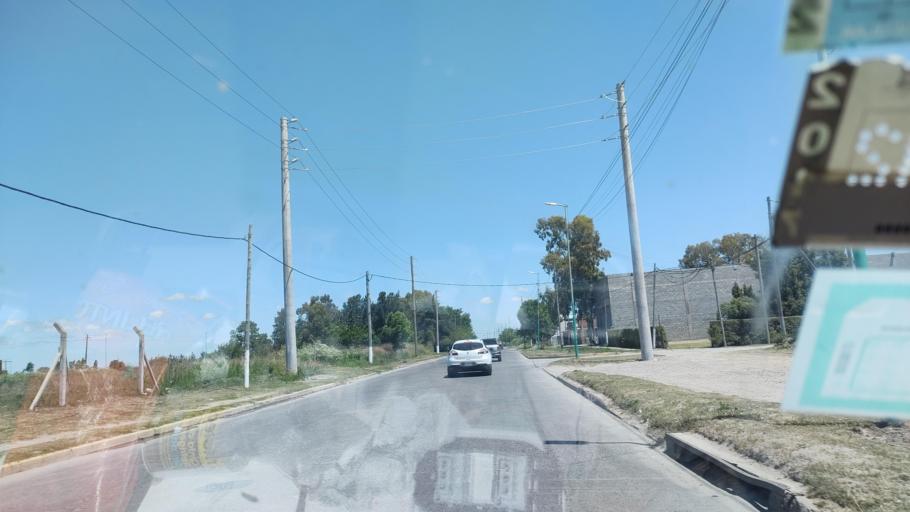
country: AR
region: Buenos Aires
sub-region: Partido de Berisso
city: Berisso
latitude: -34.8882
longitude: -57.8695
